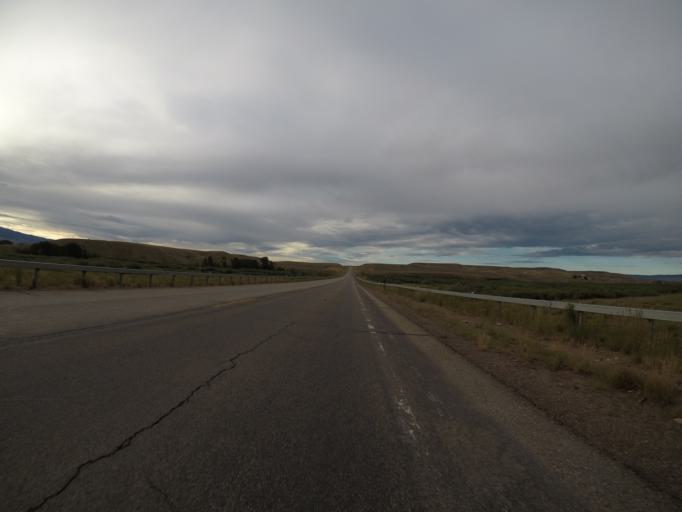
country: US
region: Wyoming
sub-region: Carbon County
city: Saratoga
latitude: 41.4292
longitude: -106.7996
